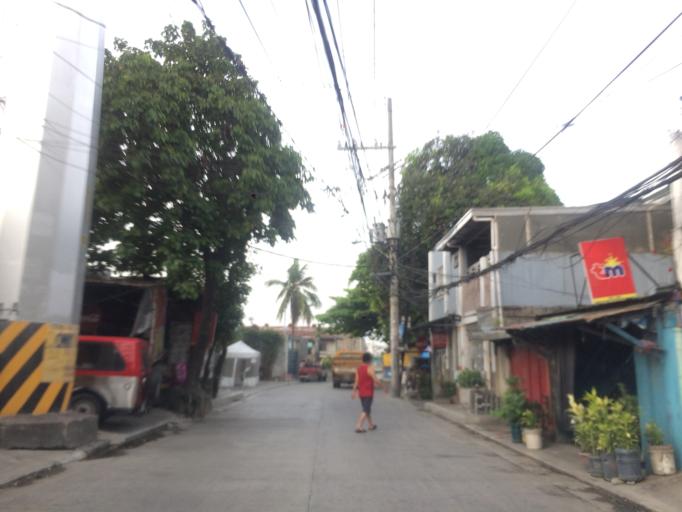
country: PH
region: Calabarzon
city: Del Monte
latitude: 14.6482
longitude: 121.0094
